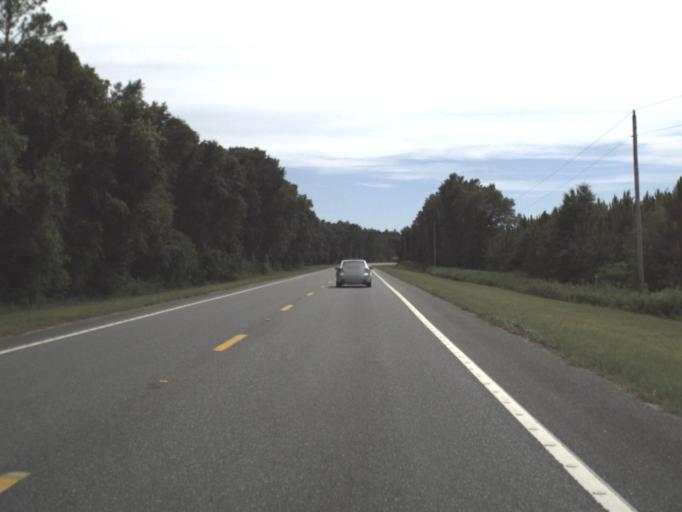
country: US
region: Florida
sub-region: Taylor County
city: Perry
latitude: 30.0861
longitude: -83.4983
